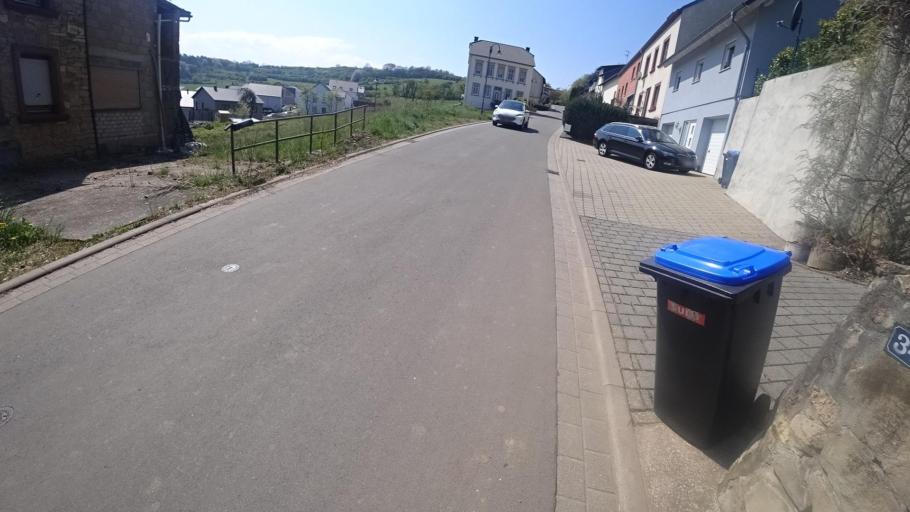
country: LU
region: Grevenmacher
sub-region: Canton de Grevenmacher
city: Mertert
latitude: 49.6802
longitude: 6.4974
